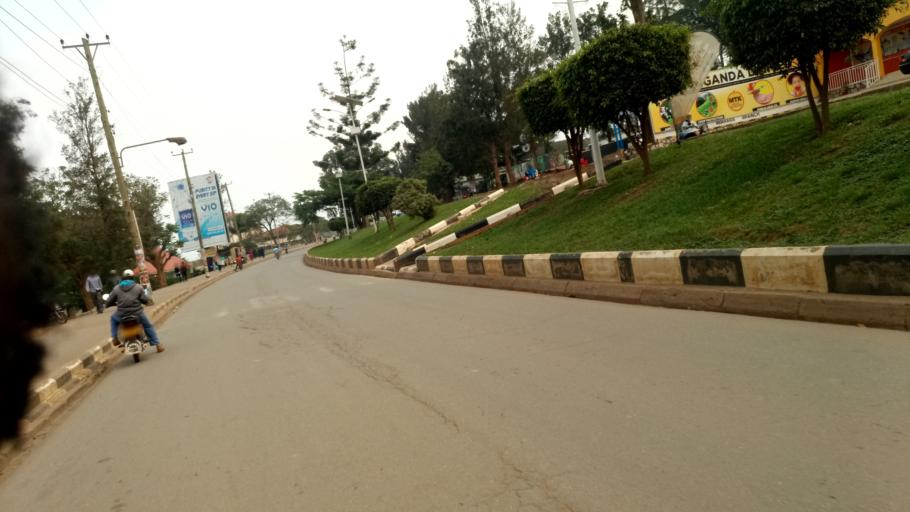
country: UG
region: Western Region
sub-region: Mbarara District
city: Mbarara
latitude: -0.6105
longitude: 30.6608
